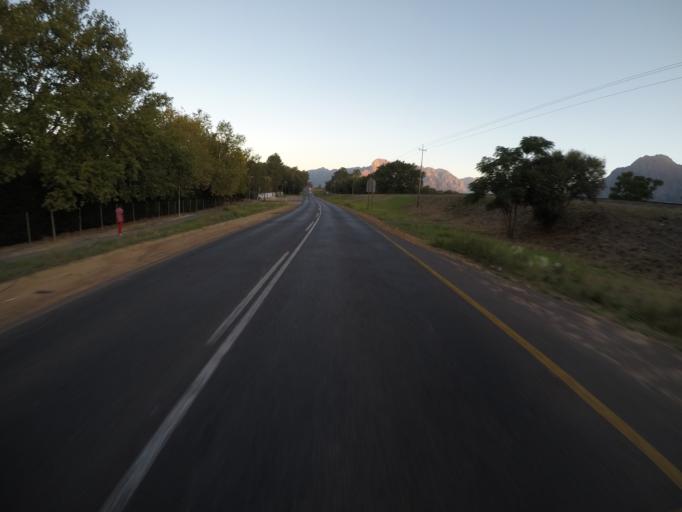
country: ZA
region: Western Cape
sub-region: Cape Winelands District Municipality
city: Paarl
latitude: -33.8376
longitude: 18.9544
